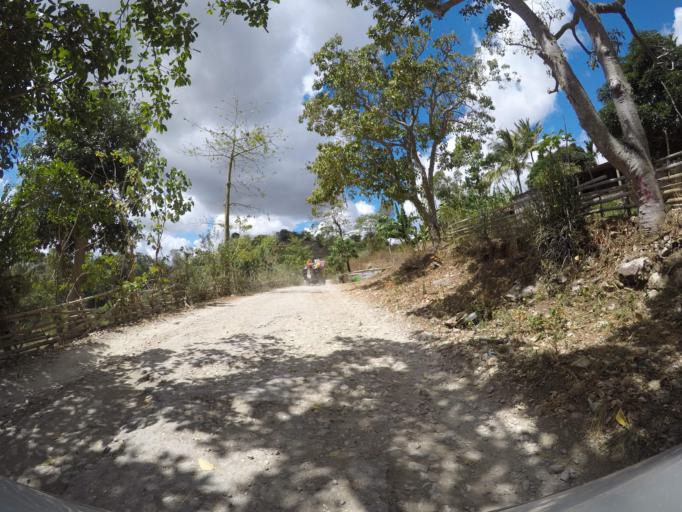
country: TL
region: Baucau
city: Baucau
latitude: -8.5122
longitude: 126.6838
